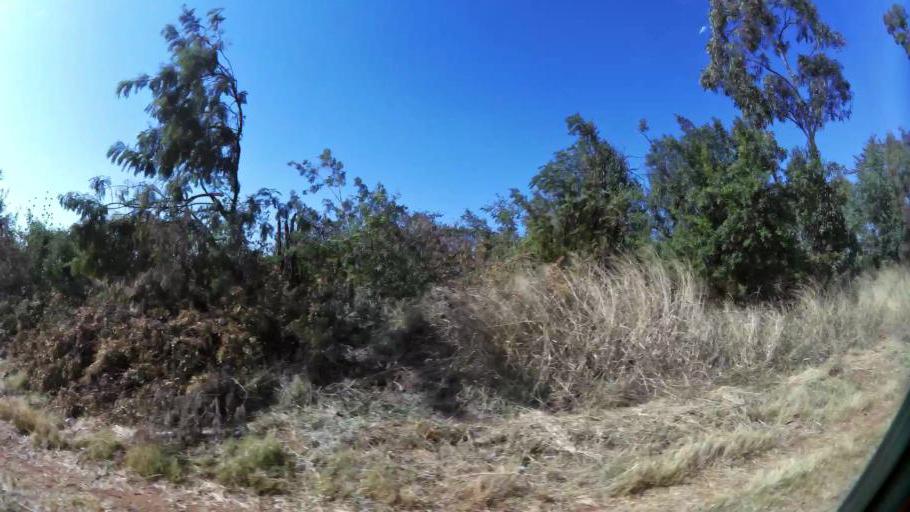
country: ZA
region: North-West
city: Ga-Rankuwa
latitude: -25.6442
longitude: 28.0899
